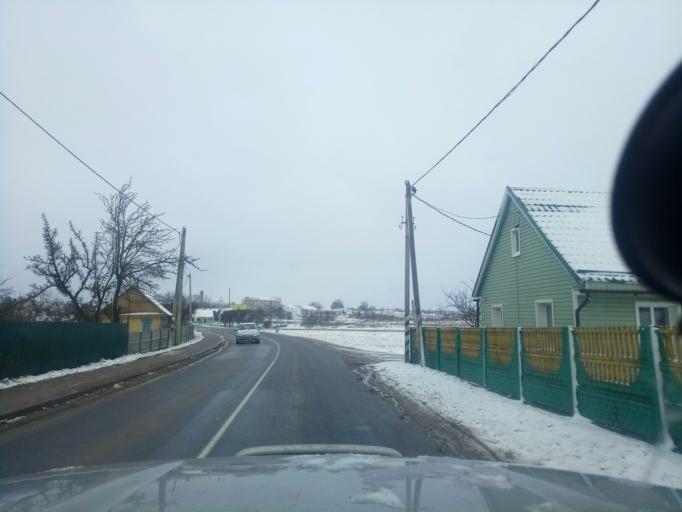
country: BY
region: Minsk
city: Tsimkavichy
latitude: 53.0685
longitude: 26.9888
